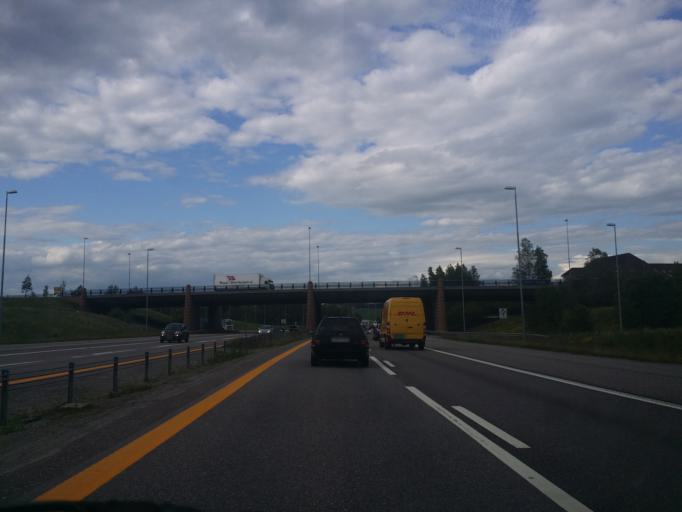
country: NO
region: Akershus
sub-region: Skedsmo
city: Lillestrom
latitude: 59.9784
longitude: 10.9938
